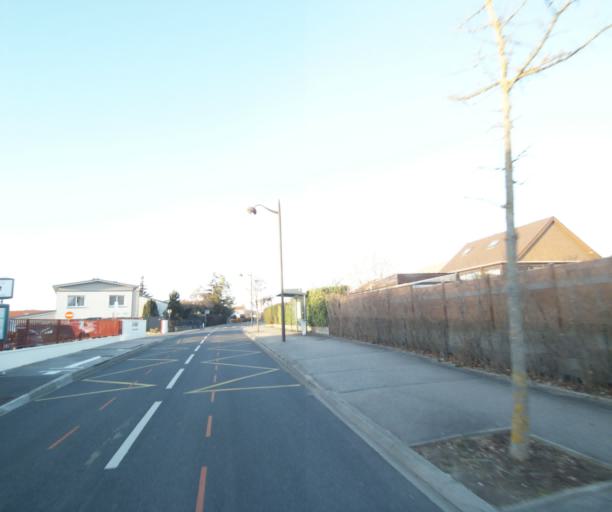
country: FR
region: Lorraine
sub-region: Departement de Meurthe-et-Moselle
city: Pulnoy
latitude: 48.7039
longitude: 6.2602
